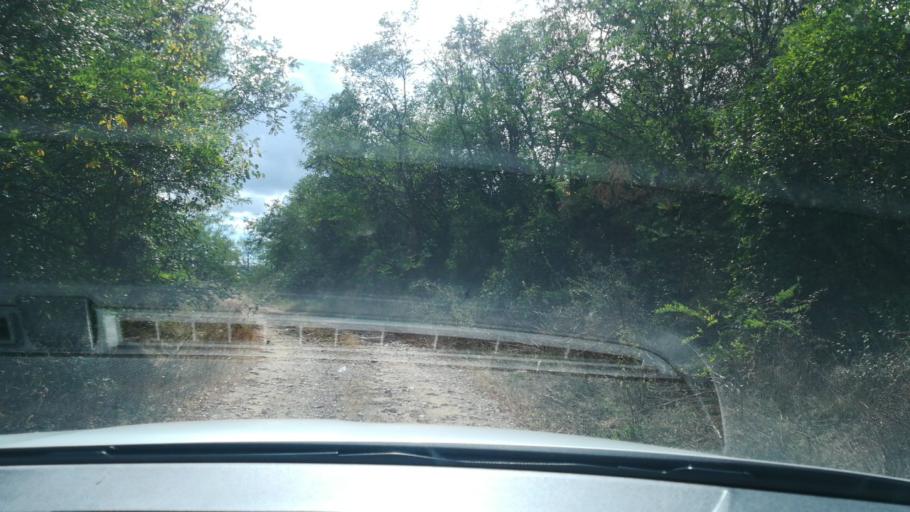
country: MK
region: Delcevo
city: Delcevo
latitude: 41.8933
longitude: 22.8052
